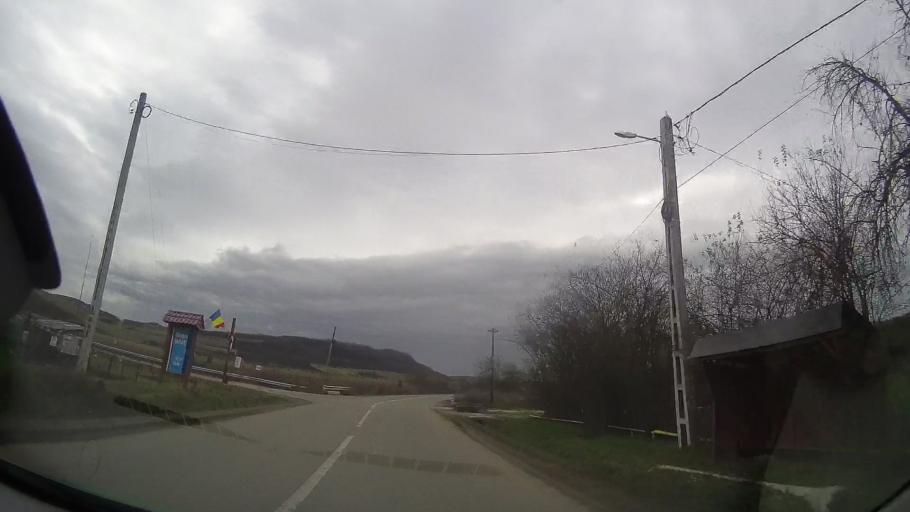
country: RO
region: Bistrita-Nasaud
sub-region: Comuna Milas
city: Milas
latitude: 46.8062
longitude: 24.4281
